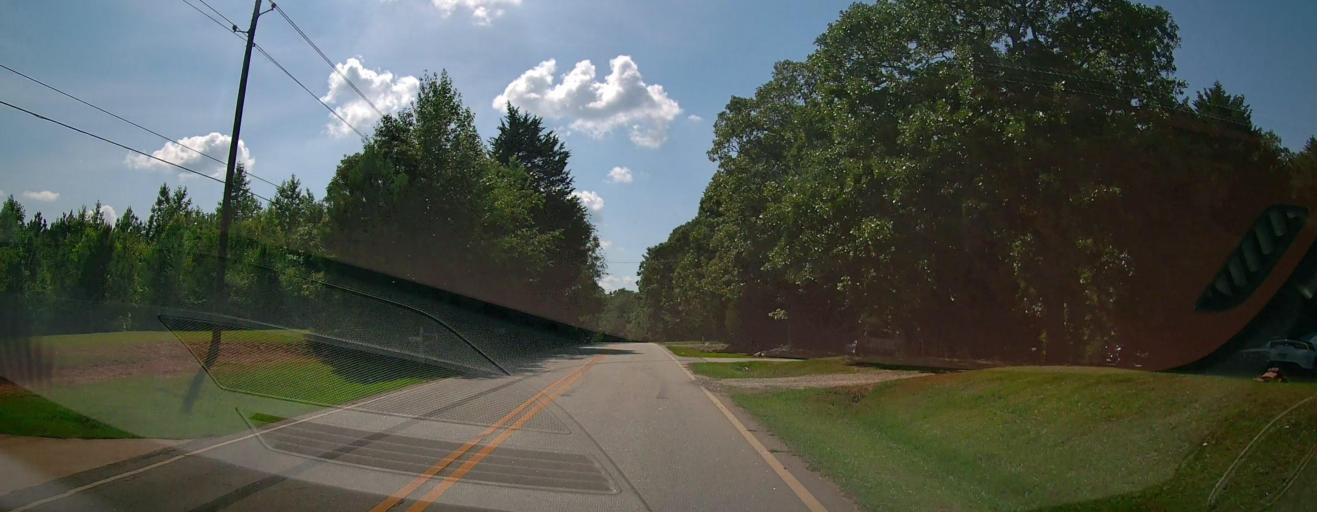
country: US
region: Georgia
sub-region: Spalding County
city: East Griffin
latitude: 33.2439
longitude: -84.1716
